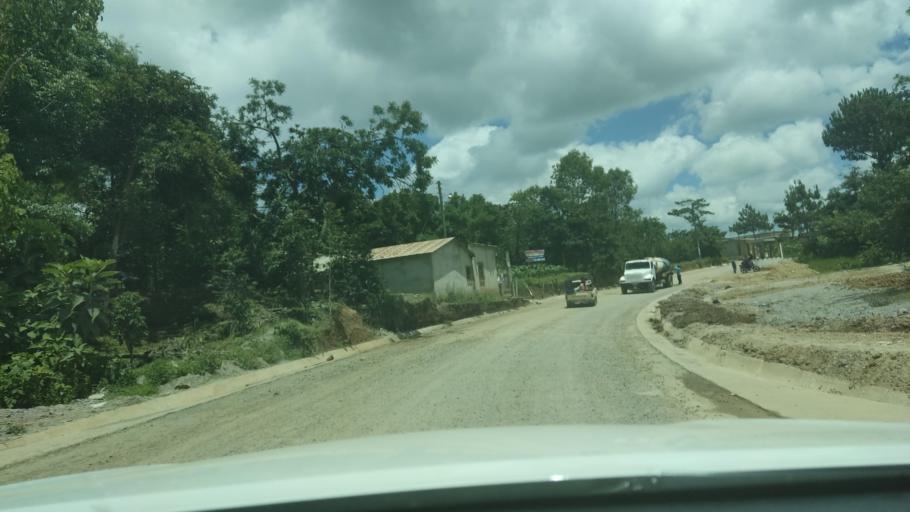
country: GT
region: Chimaltenango
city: San Martin Jilotepeque
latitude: 14.7914
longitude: -90.8076
